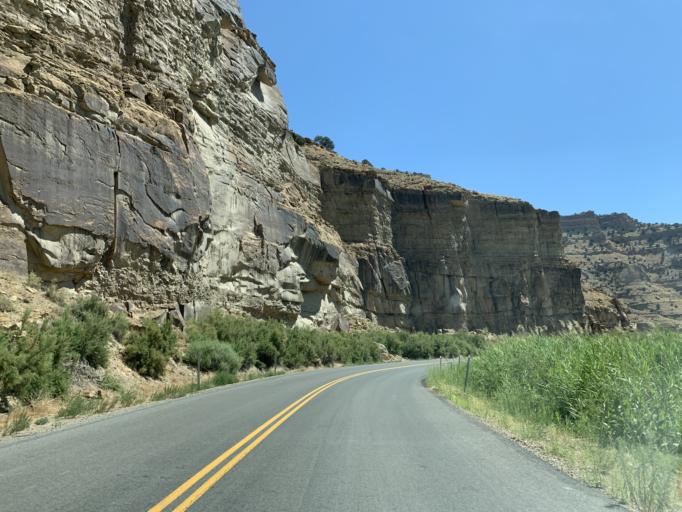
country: US
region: Utah
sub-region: Carbon County
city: East Carbon City
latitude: 39.8135
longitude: -110.2815
